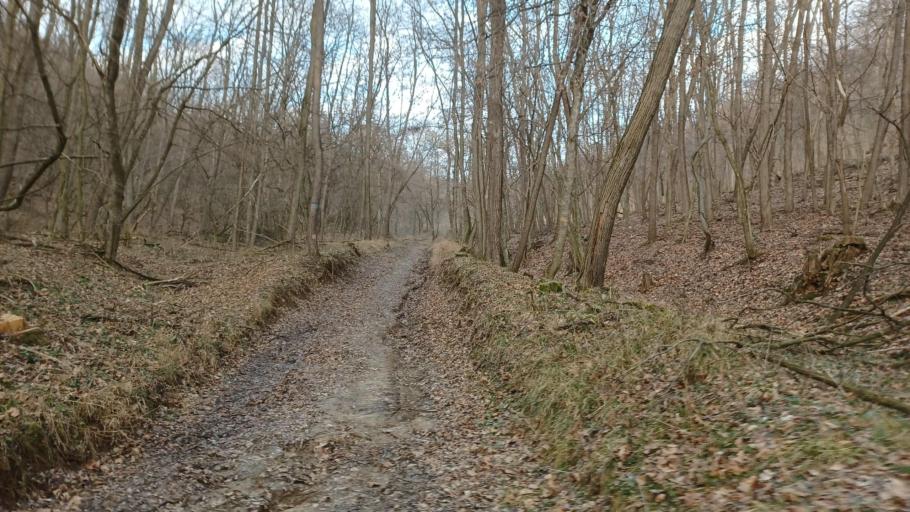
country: HU
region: Tolna
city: Szentgalpuszta
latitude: 46.3052
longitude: 18.6175
